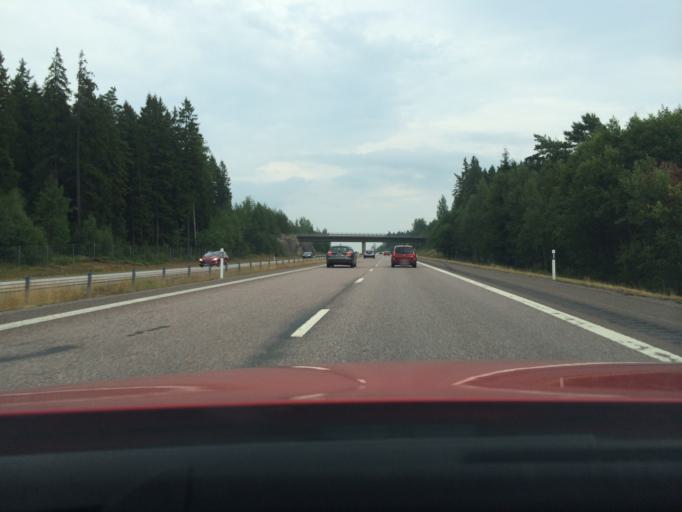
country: SE
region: OEstergoetland
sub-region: Norrkopings Kommun
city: Krokek
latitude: 58.7440
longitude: 16.4985
